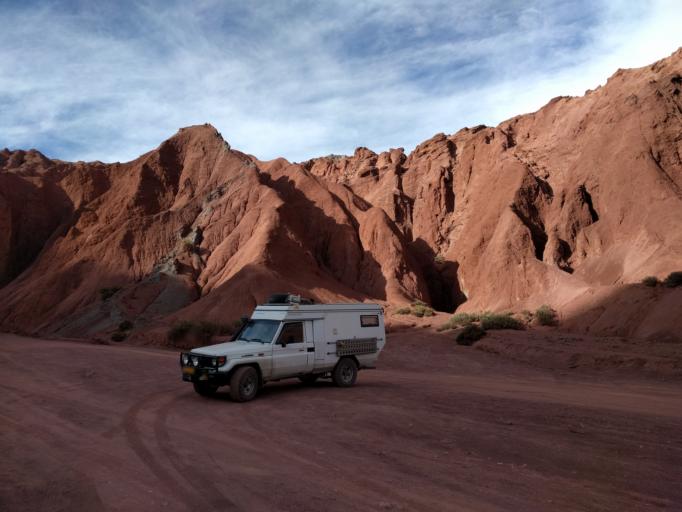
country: CL
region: Antofagasta
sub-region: Provincia de El Loa
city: San Pedro de Atacama
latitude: -22.6321
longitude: -68.2448
